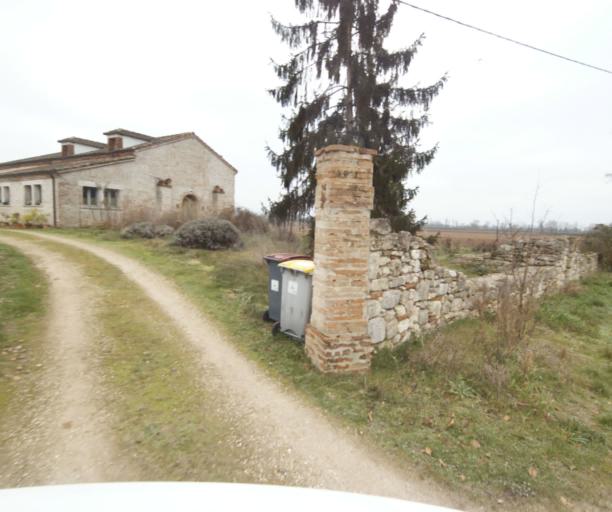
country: FR
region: Midi-Pyrenees
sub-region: Departement du Tarn-et-Garonne
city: Moissac
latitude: 44.1012
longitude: 1.1294
